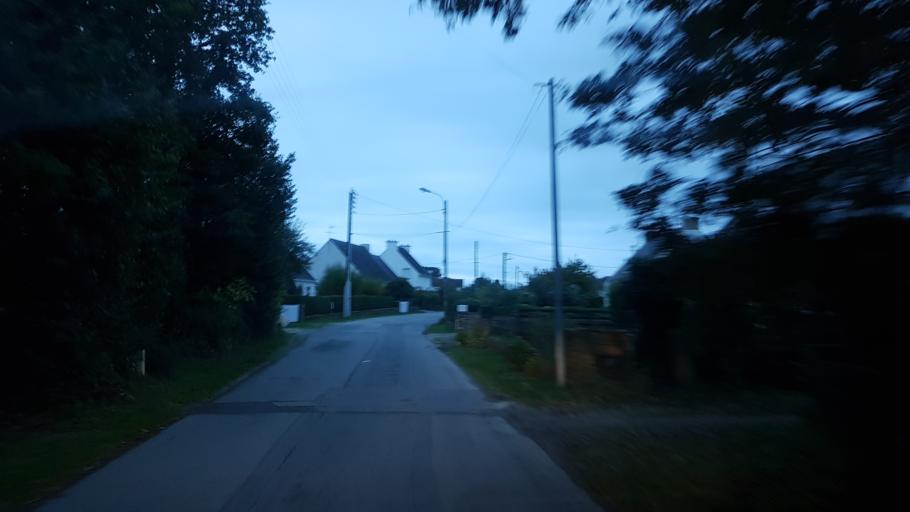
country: FR
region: Brittany
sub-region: Departement du Morbihan
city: Sarzeau
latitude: 47.5416
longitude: -2.8094
